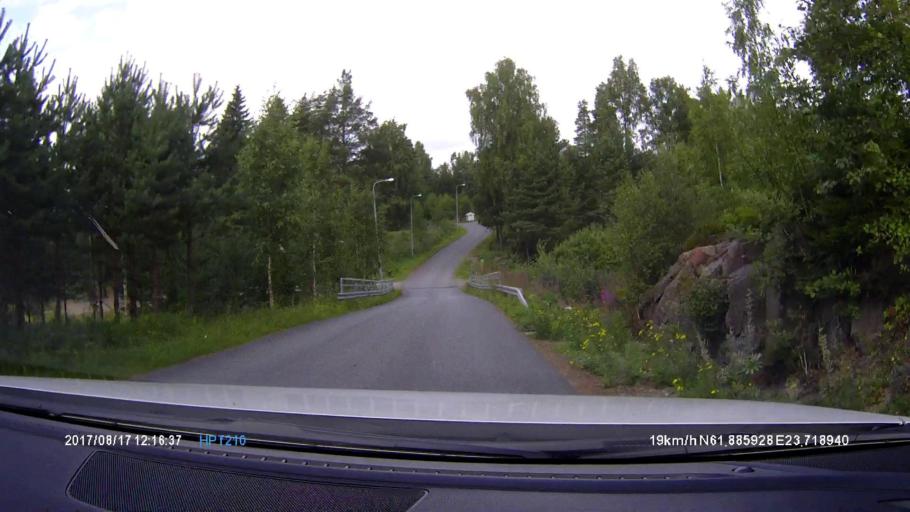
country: FI
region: Pirkanmaa
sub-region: Tampere
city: Kuru
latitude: 61.8861
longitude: 23.7187
